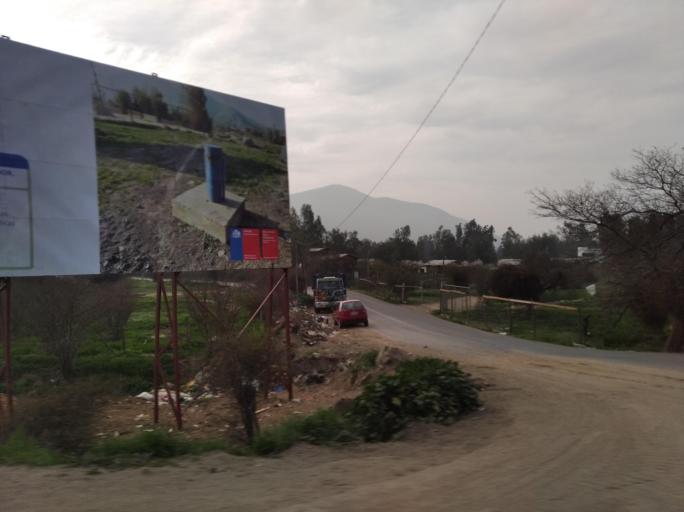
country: CL
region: Santiago Metropolitan
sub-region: Provincia de Chacabuco
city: Lampa
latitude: -33.2655
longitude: -70.8962
